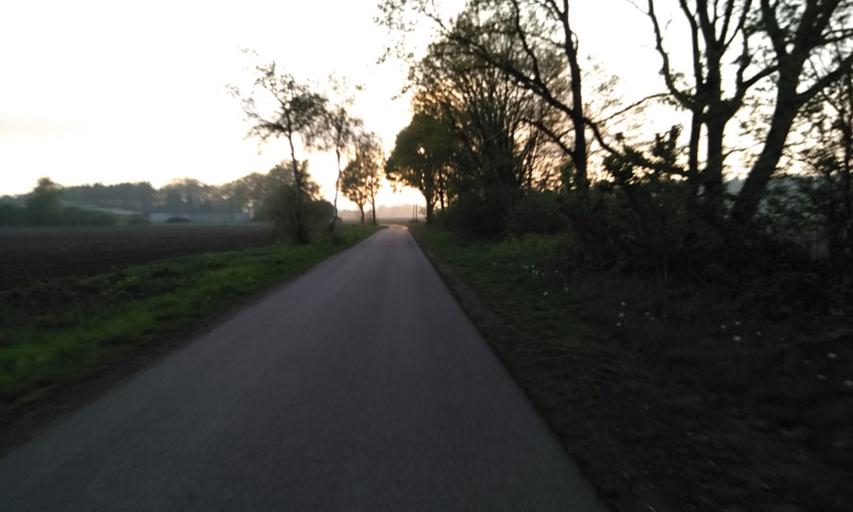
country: DE
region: Lower Saxony
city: Deinste
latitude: 53.4991
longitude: 9.4231
